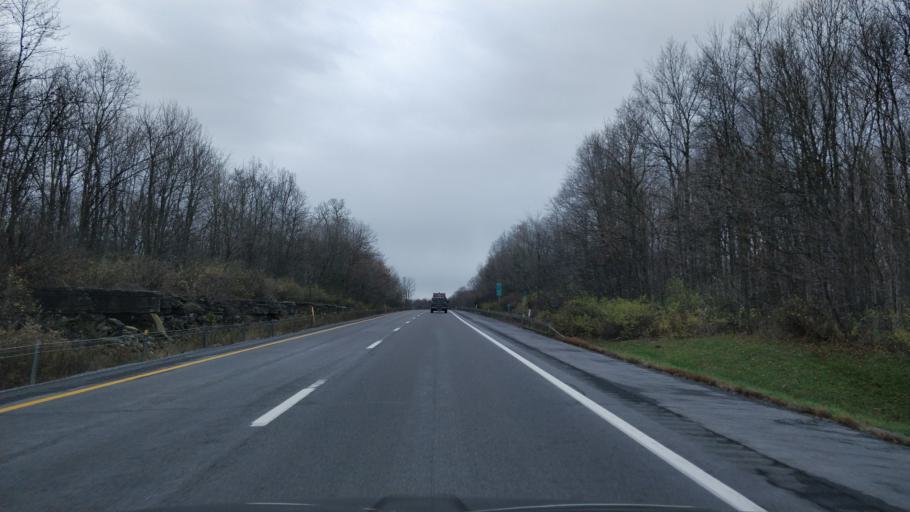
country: US
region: New York
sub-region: Jefferson County
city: Calcium
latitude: 44.1161
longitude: -75.8906
